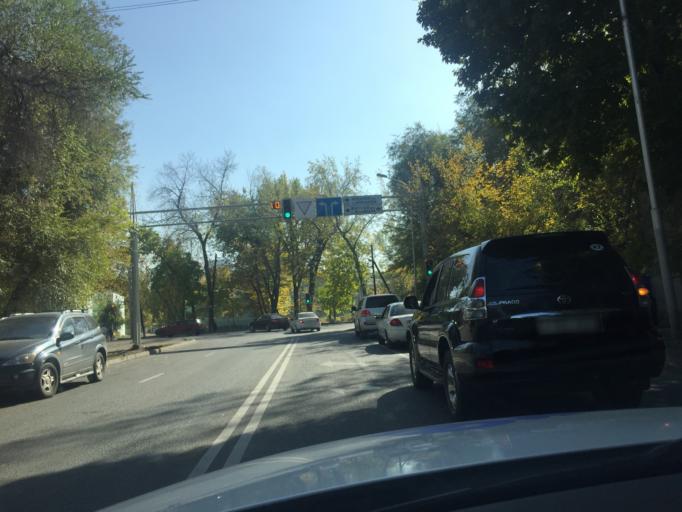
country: KZ
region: Almaty Qalasy
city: Almaty
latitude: 43.2462
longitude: 76.9124
